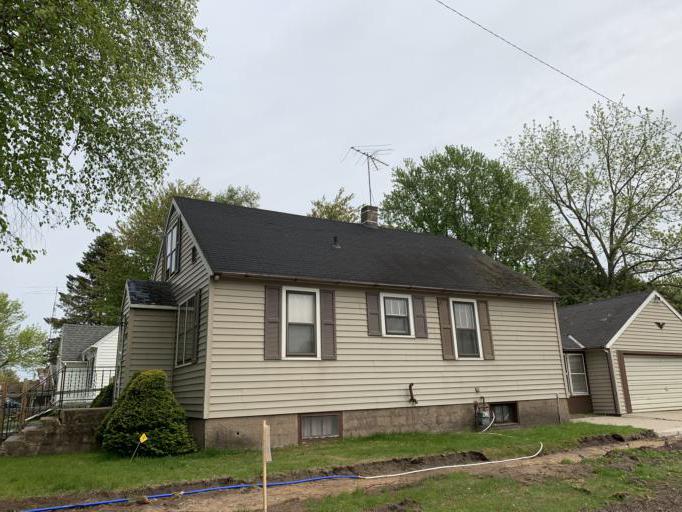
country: US
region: Wisconsin
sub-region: Marinette County
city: Marinette
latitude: 45.1021
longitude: -87.6462
